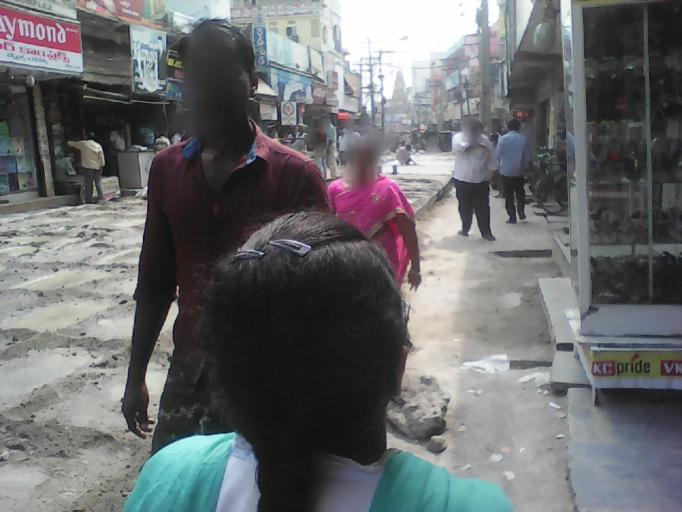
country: IN
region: Andhra Pradesh
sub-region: Guntur
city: Bhattiprolu
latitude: 16.2381
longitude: 80.6496
